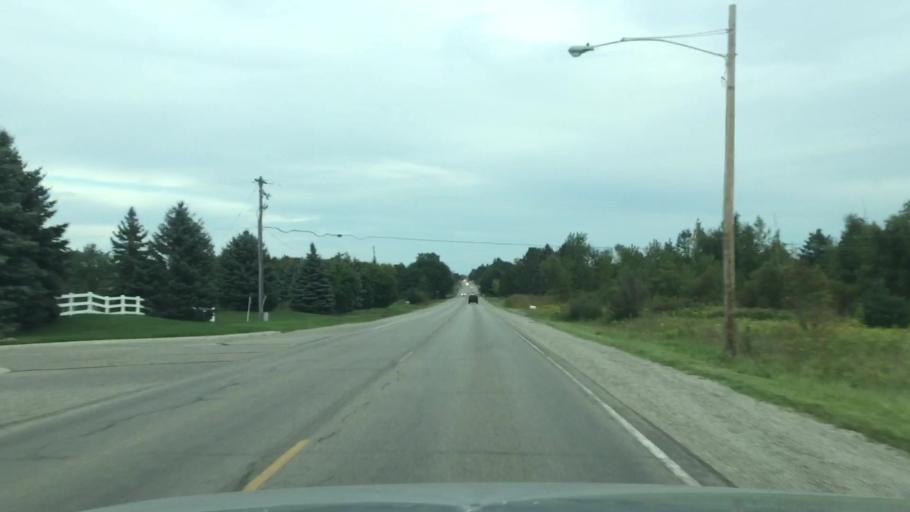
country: US
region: Michigan
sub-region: Genesee County
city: Lake Fenton
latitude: 42.8860
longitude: -83.6711
